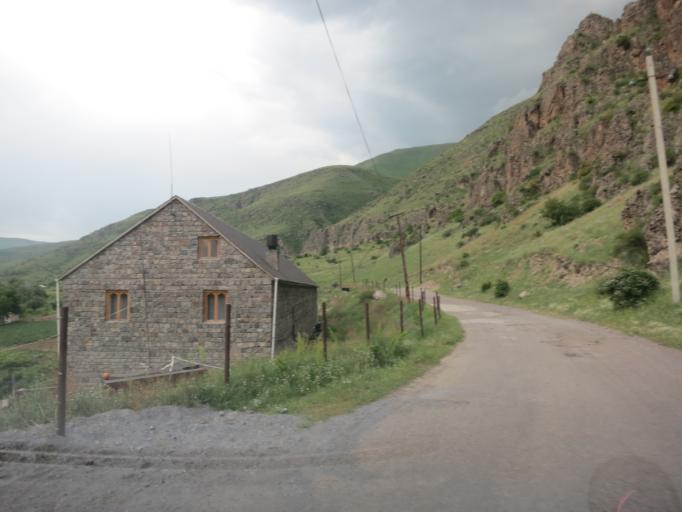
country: TR
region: Ardahan
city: Kurtkale
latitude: 41.3691
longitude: 43.2552
